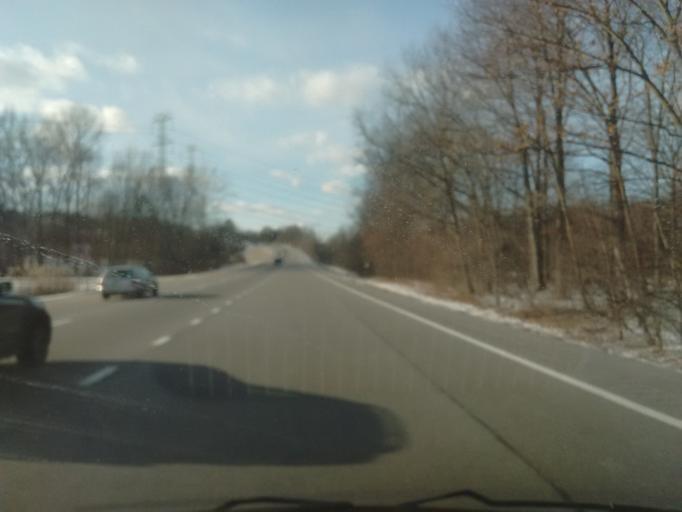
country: US
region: New York
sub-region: Dutchess County
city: Brinckerhoff
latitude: 41.5318
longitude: -73.8222
